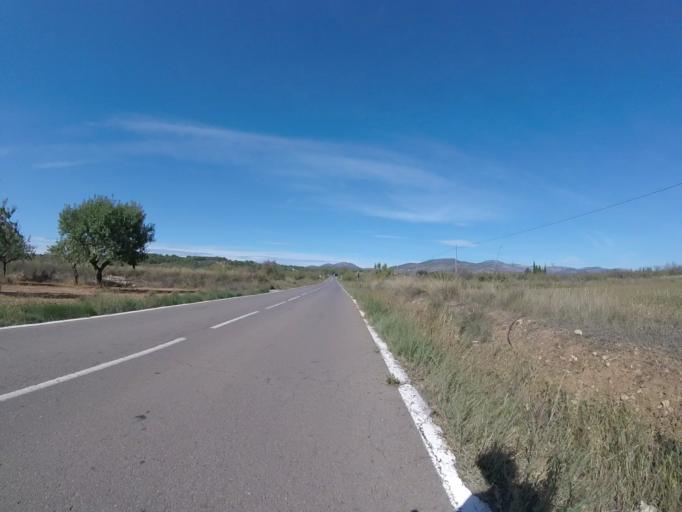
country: ES
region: Valencia
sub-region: Provincia de Castello
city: Benlloch
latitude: 40.2180
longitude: 0.0171
